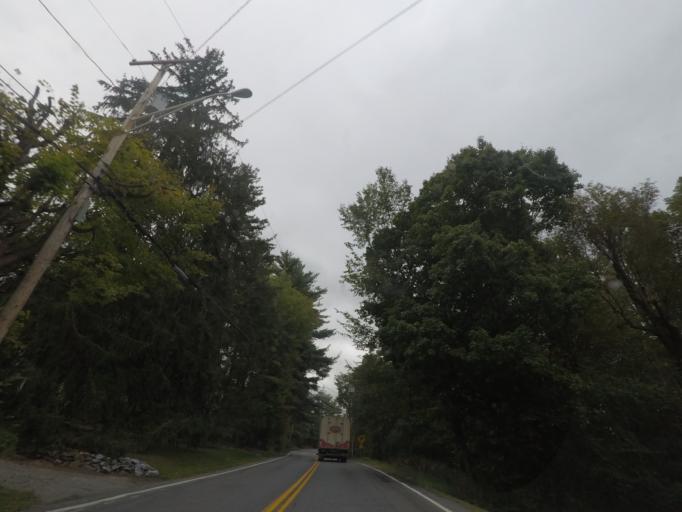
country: US
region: New York
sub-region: Rensselaer County
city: Hoosick Falls
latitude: 42.9299
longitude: -73.3469
